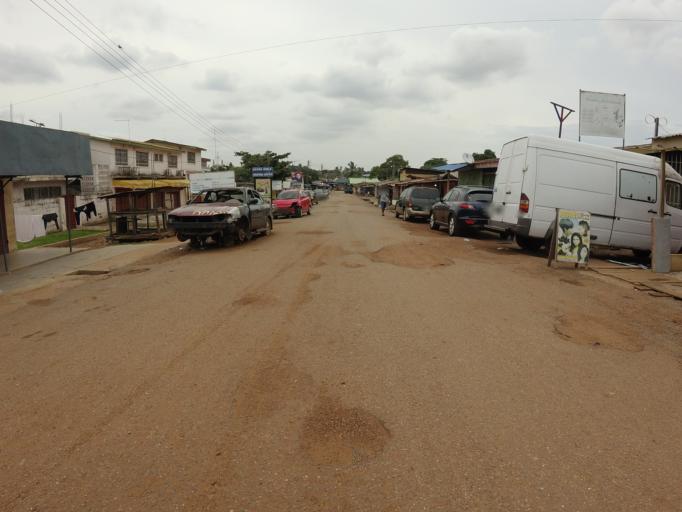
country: GH
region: Greater Accra
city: Dome
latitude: 5.6066
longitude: -0.2254
